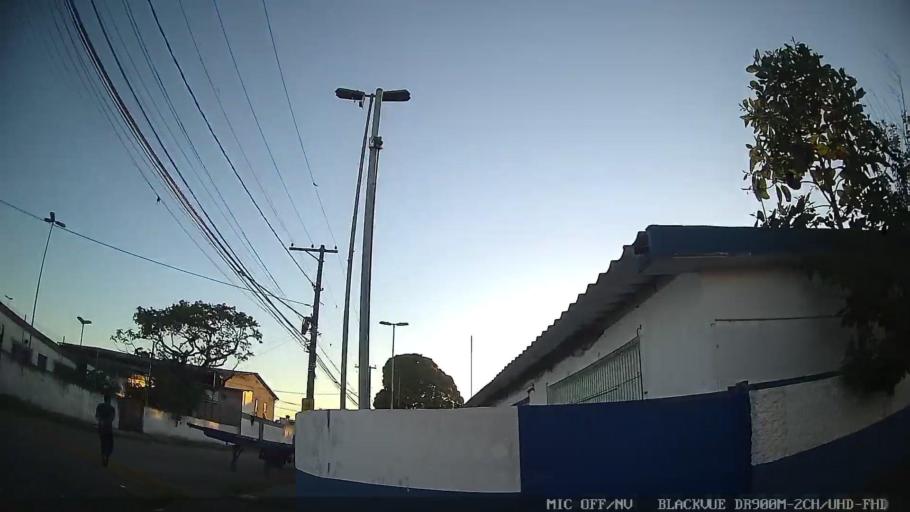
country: BR
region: Sao Paulo
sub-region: Guaruja
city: Guaruja
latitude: -23.9576
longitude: -46.2842
